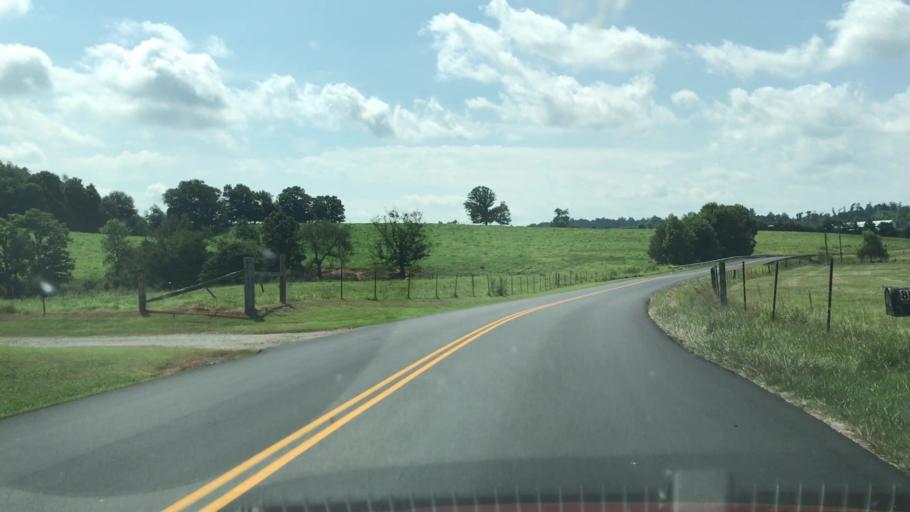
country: US
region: Kentucky
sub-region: Monroe County
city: Tompkinsville
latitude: 36.7768
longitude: -85.8000
